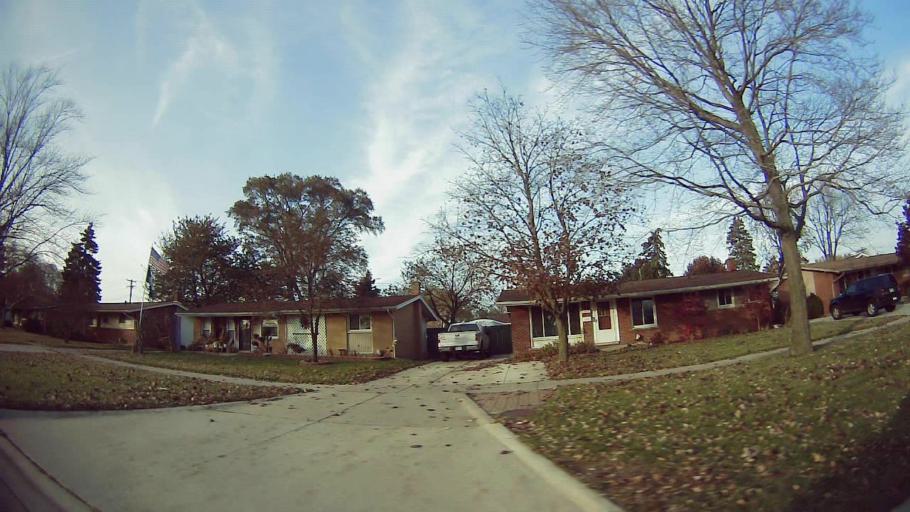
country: US
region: Michigan
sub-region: Oakland County
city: Clawson
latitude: 42.5197
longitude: -83.1228
